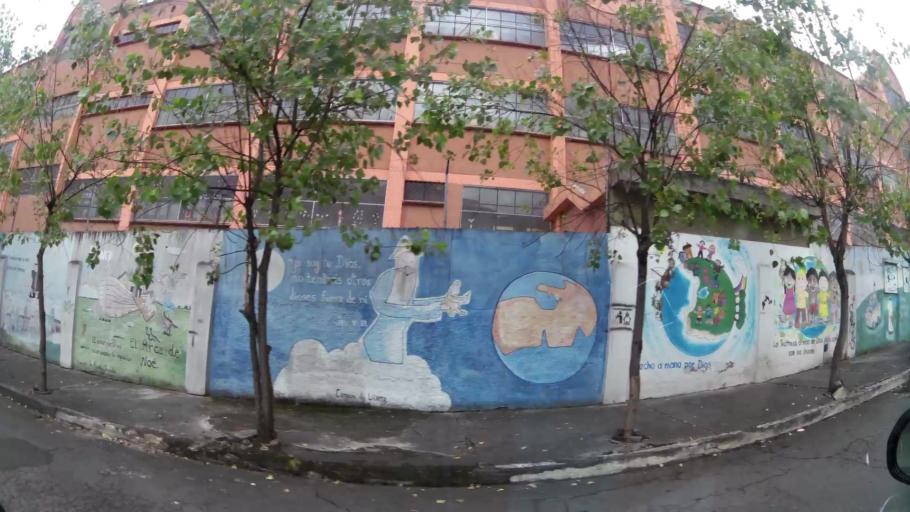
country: EC
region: Pichincha
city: Quito
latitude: -0.1971
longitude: -78.5101
